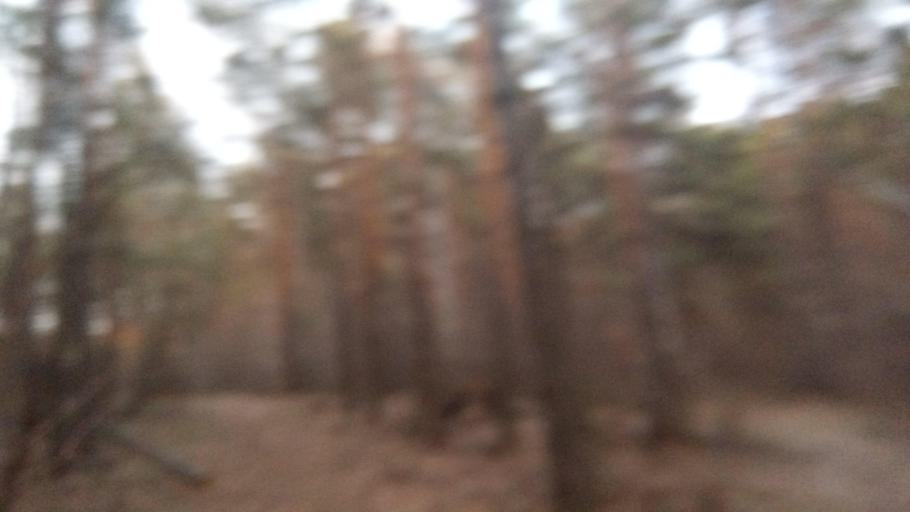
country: RU
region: Chelyabinsk
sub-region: Gorod Chelyabinsk
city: Chelyabinsk
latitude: 55.1561
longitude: 61.3363
